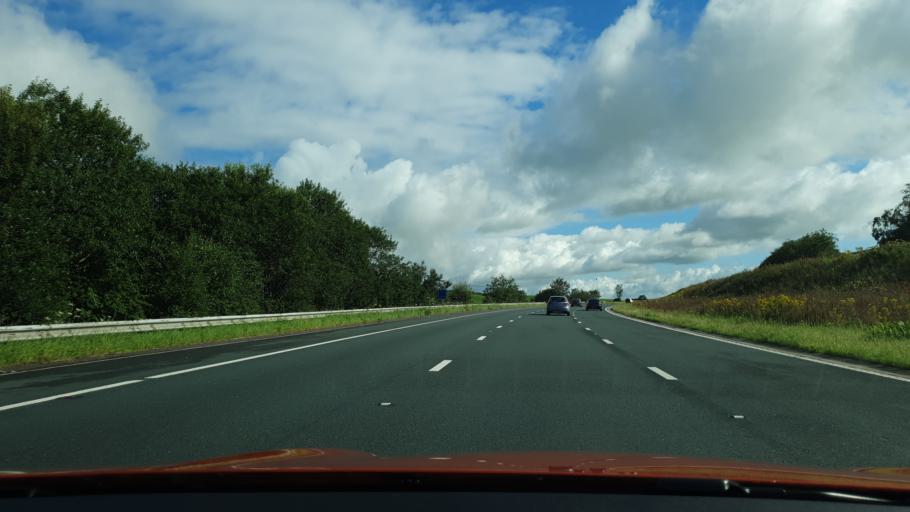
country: GB
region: England
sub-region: Cumbria
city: Kendal
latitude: 54.2653
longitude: -2.6844
